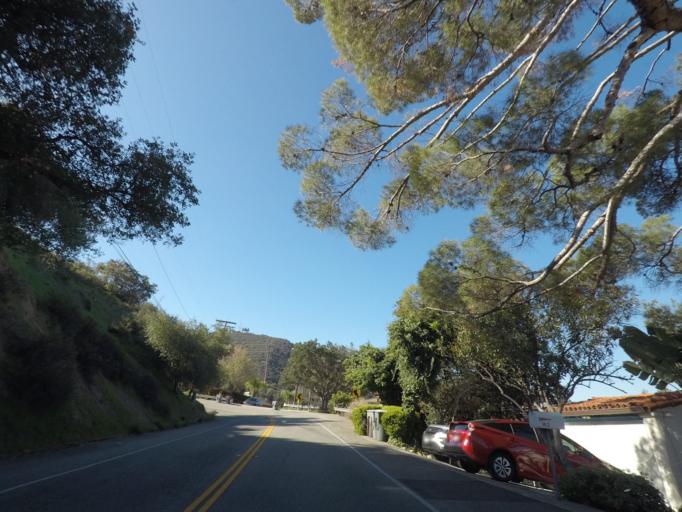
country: US
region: California
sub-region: Los Angeles County
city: La Canada Flintridge
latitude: 34.1717
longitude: -118.1946
